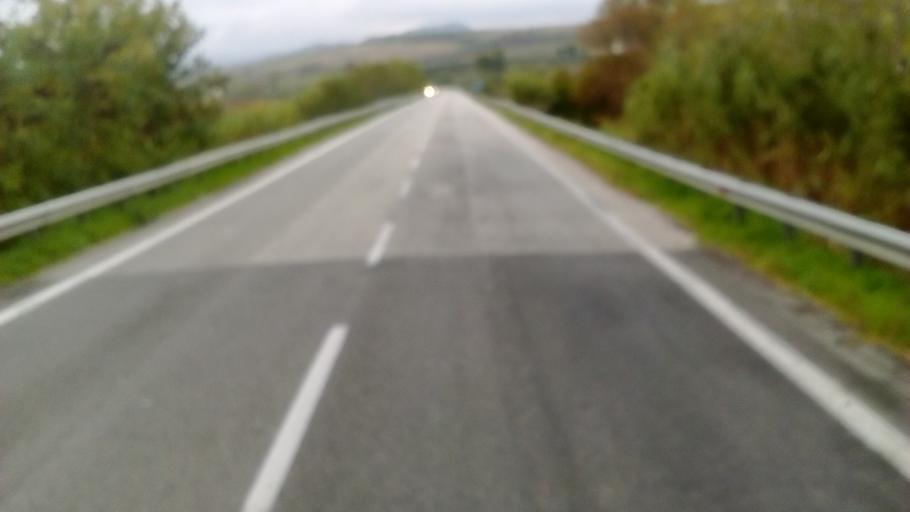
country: IT
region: Abruzzo
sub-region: Provincia di Chieti
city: San Salvo
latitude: 42.0268
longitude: 14.7384
